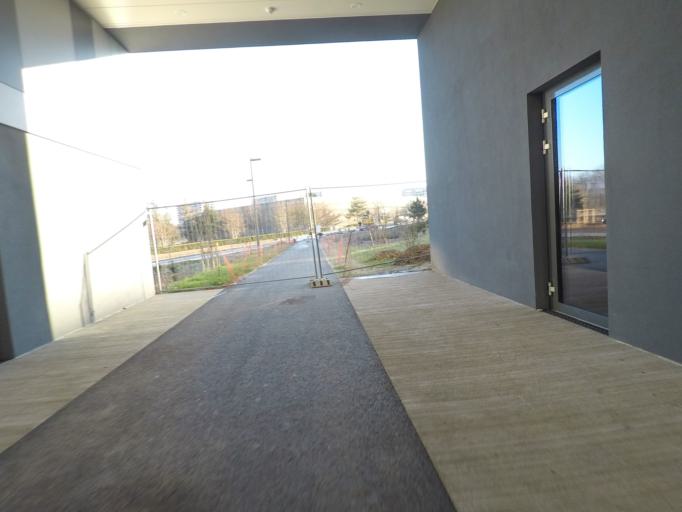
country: CH
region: Geneva
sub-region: Geneva
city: Meyrin
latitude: 46.2327
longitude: 6.0723
